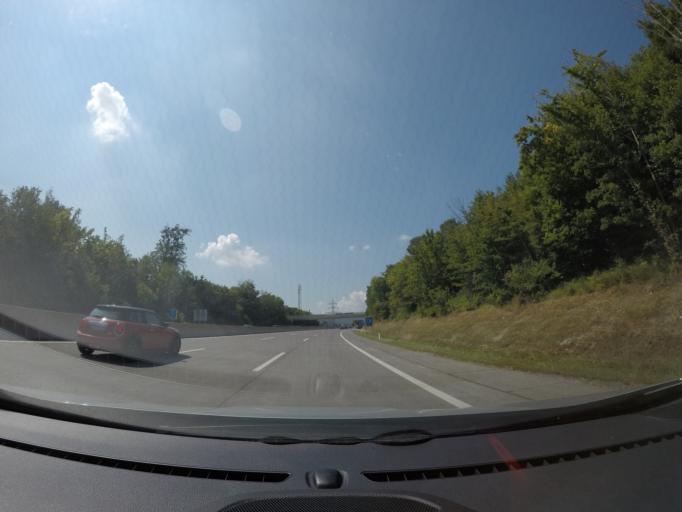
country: AT
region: Lower Austria
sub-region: Politischer Bezirk Wien-Umgebung
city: Purkersdorf
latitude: 48.1942
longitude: 16.2048
